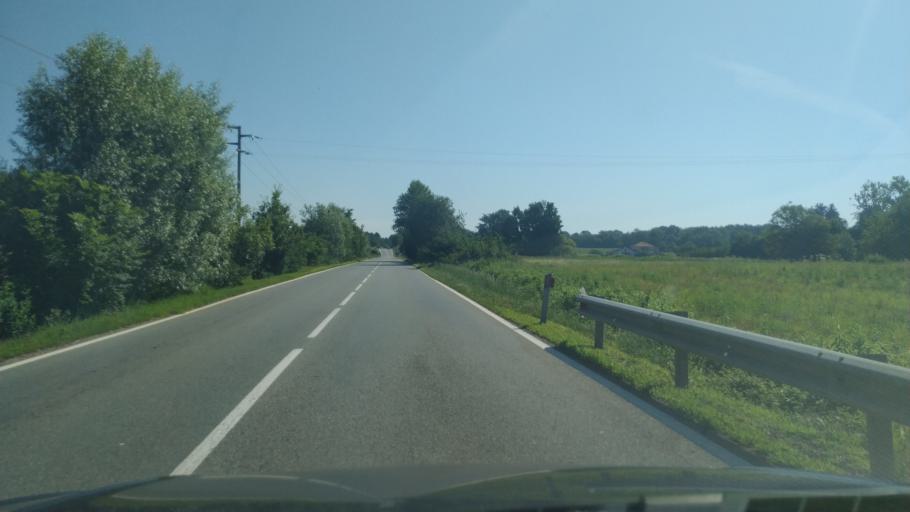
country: IT
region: Piedmont
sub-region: Provincia di Novara
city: Cavallirio
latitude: 45.6487
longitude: 8.3972
